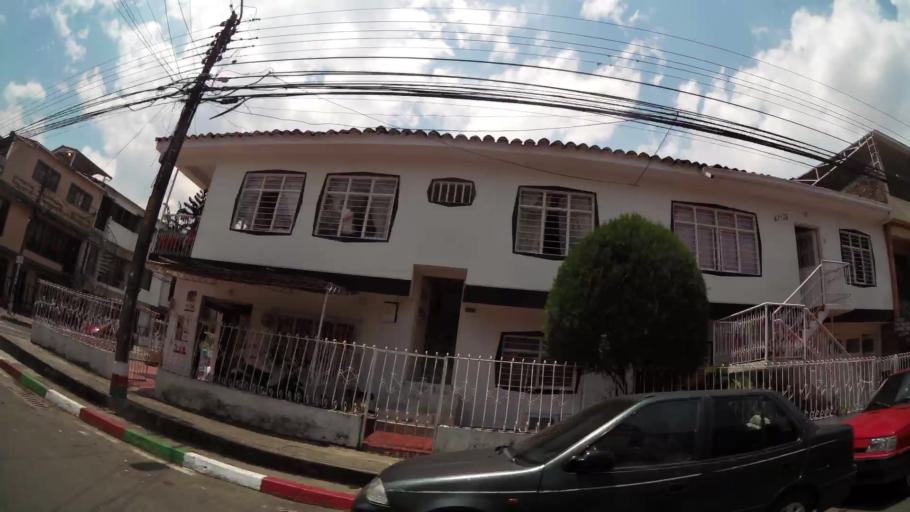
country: CO
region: Valle del Cauca
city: Cali
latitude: 3.4109
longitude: -76.5318
